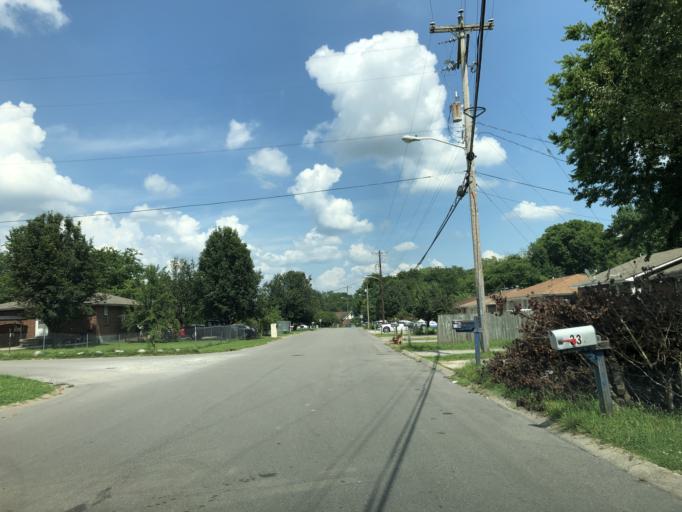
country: US
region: Tennessee
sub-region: Davidson County
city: Oak Hill
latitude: 36.1168
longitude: -86.7348
